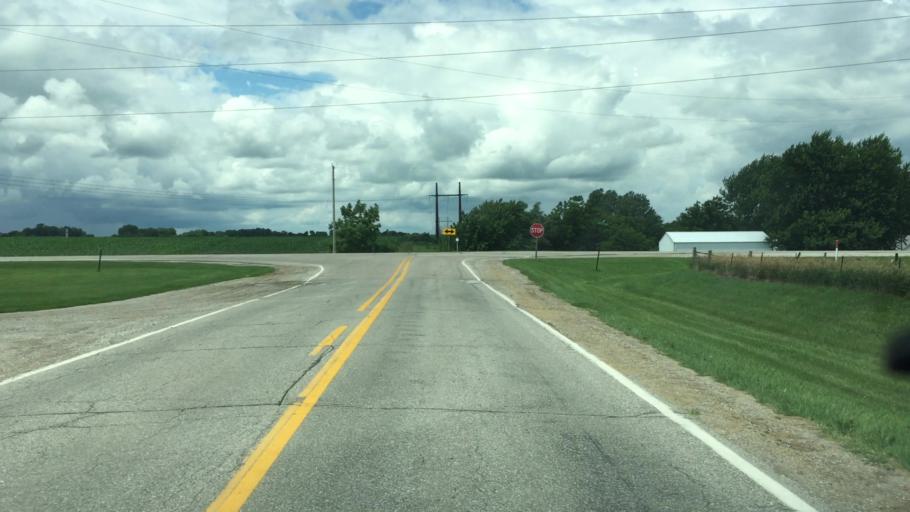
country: US
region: Iowa
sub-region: Jasper County
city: Monroe
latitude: 41.5736
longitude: -93.0961
